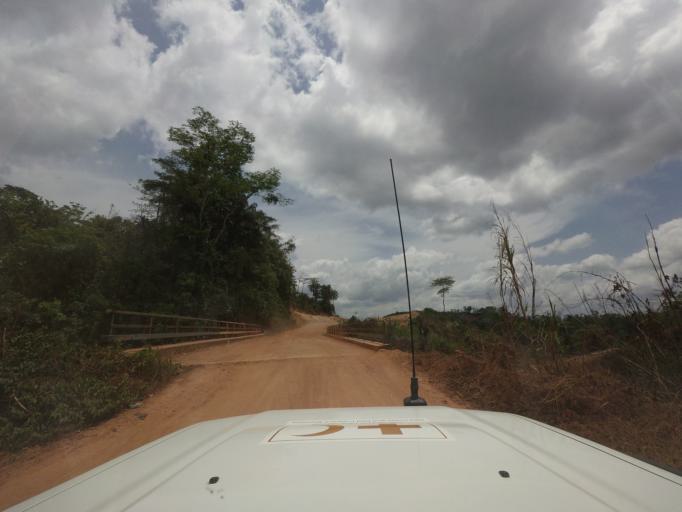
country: LR
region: Nimba
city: Sanniquellie
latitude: 7.2616
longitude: -8.8488
